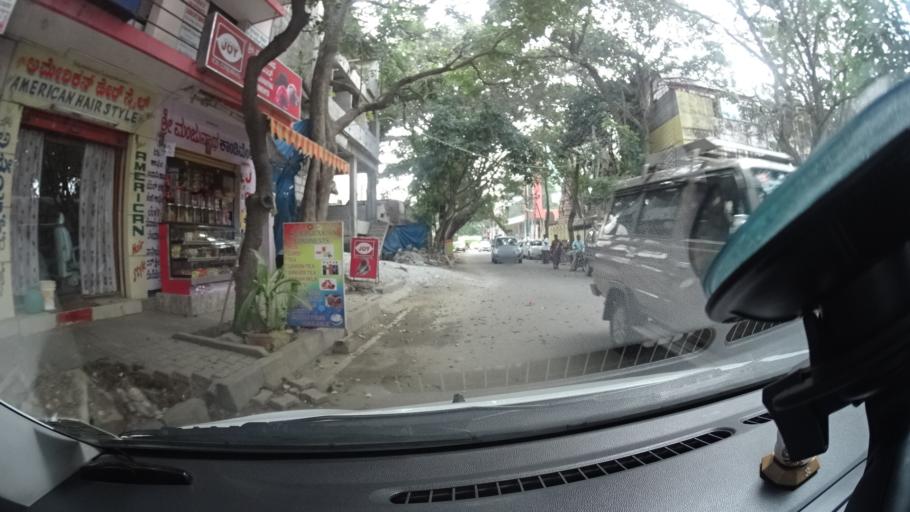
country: IN
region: Karnataka
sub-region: Bangalore Urban
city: Yelahanka
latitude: 13.0975
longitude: 77.5830
